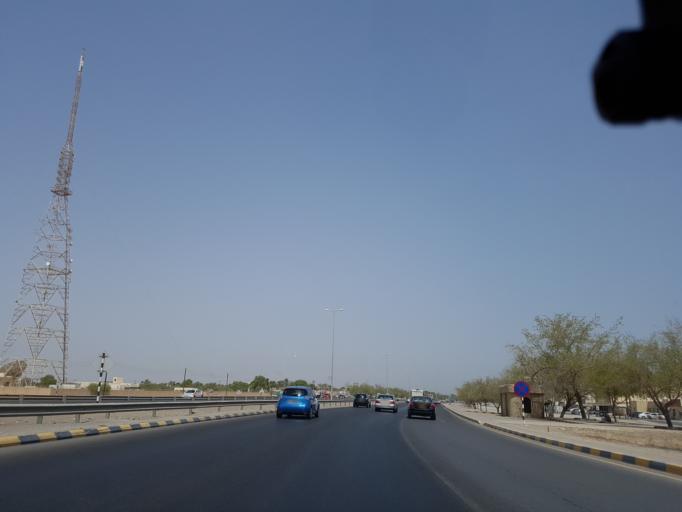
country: OM
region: Al Batinah
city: Saham
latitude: 24.1434
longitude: 56.8752
